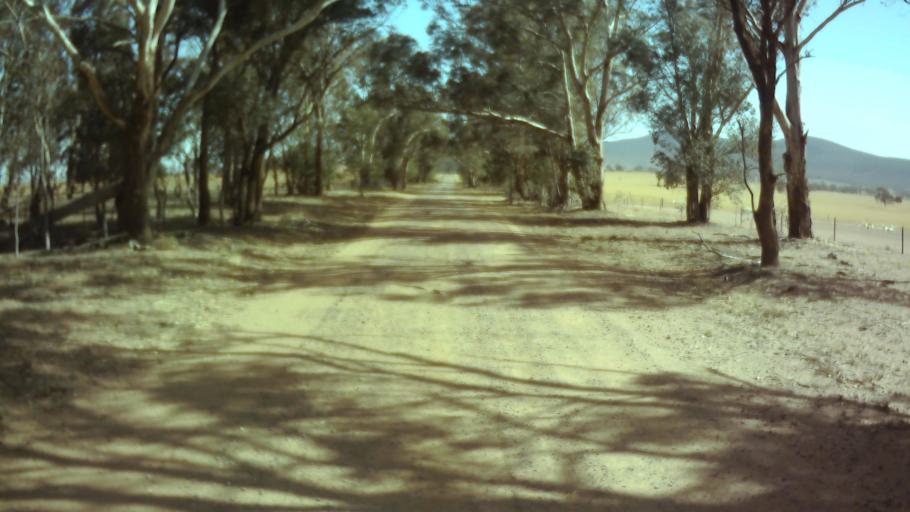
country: AU
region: New South Wales
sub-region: Weddin
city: Grenfell
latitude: -33.8487
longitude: 148.0168
